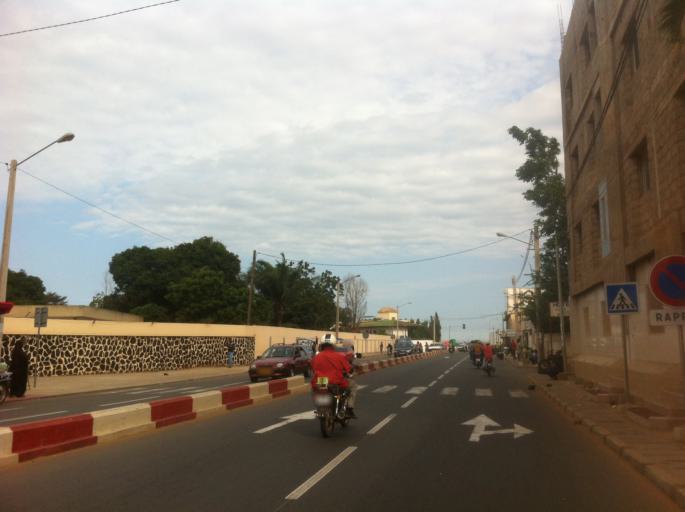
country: TG
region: Maritime
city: Lome
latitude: 6.1430
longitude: 1.2070
